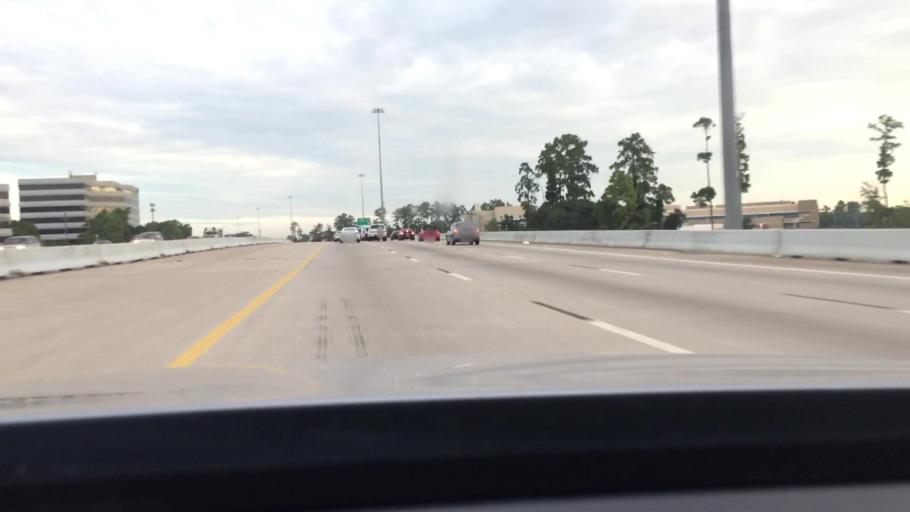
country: US
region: Texas
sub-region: Harris County
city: Oak Cliff Place
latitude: 29.9864
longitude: -95.5708
